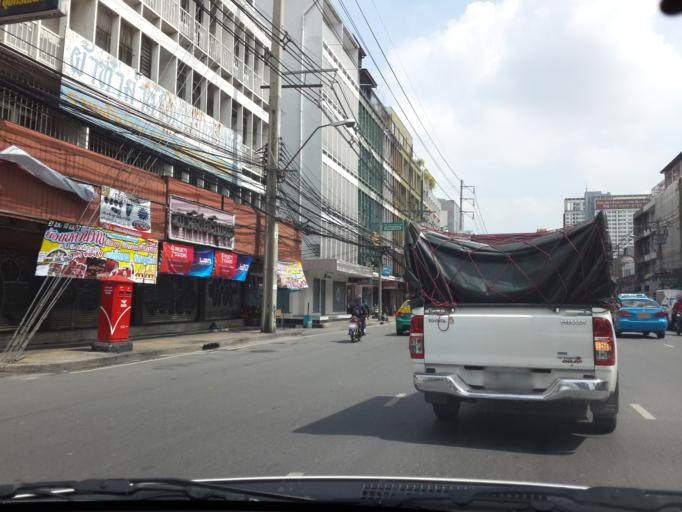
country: TH
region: Bangkok
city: Ratchathewi
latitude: 13.7567
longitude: 100.5424
